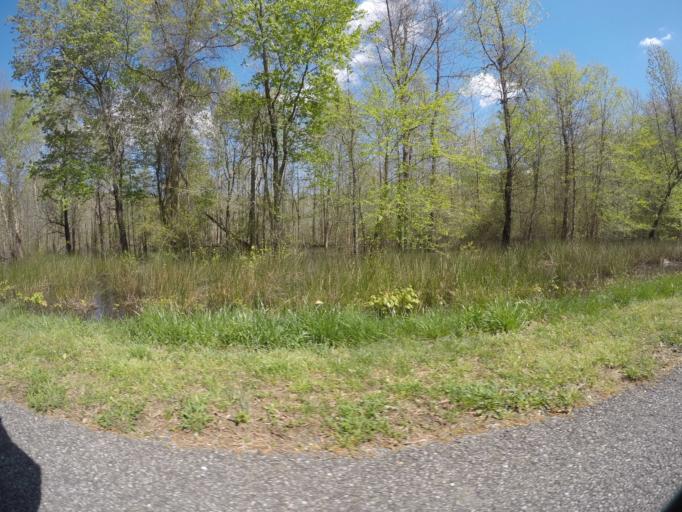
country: US
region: Maryland
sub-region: Charles County
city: Potomac Heights
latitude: 38.5919
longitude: -77.1138
